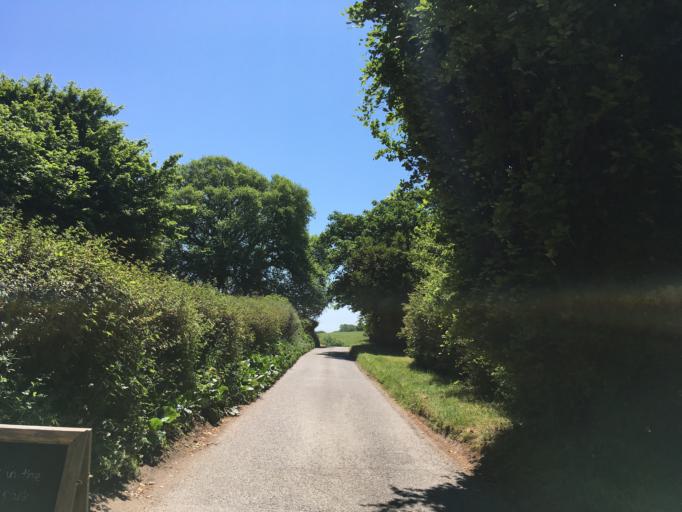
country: GB
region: England
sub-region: Devon
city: Dartmouth
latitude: 50.3495
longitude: -3.5371
